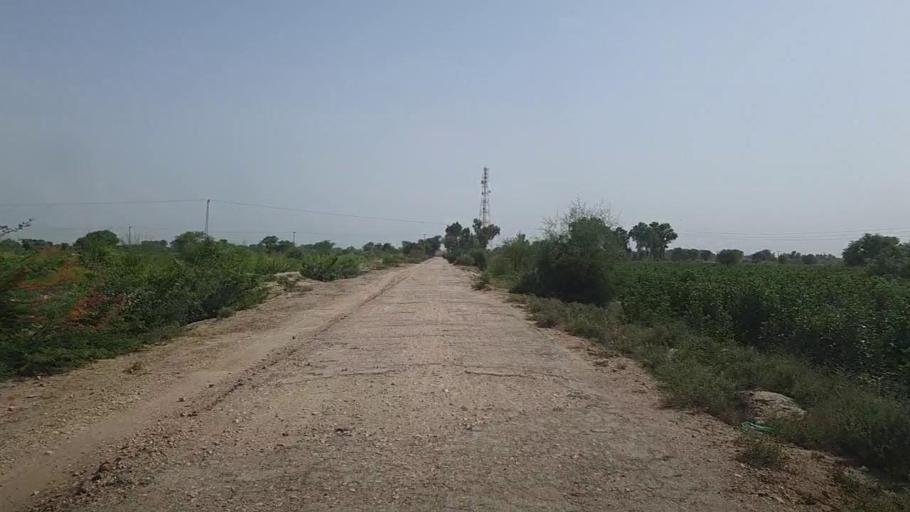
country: PK
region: Sindh
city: Pad Idan
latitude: 26.7831
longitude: 68.3238
